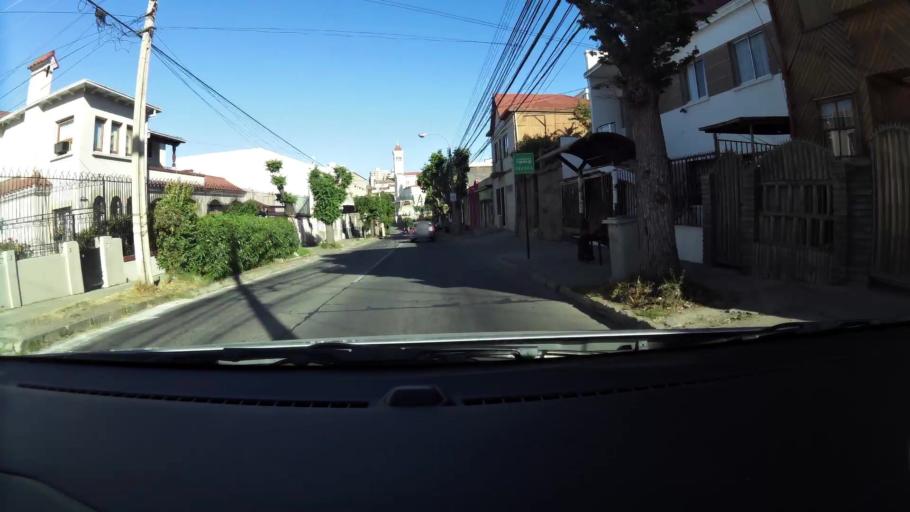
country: CL
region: Valparaiso
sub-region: Provincia de Valparaiso
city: Vina del Mar
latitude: -33.0279
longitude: -71.5642
